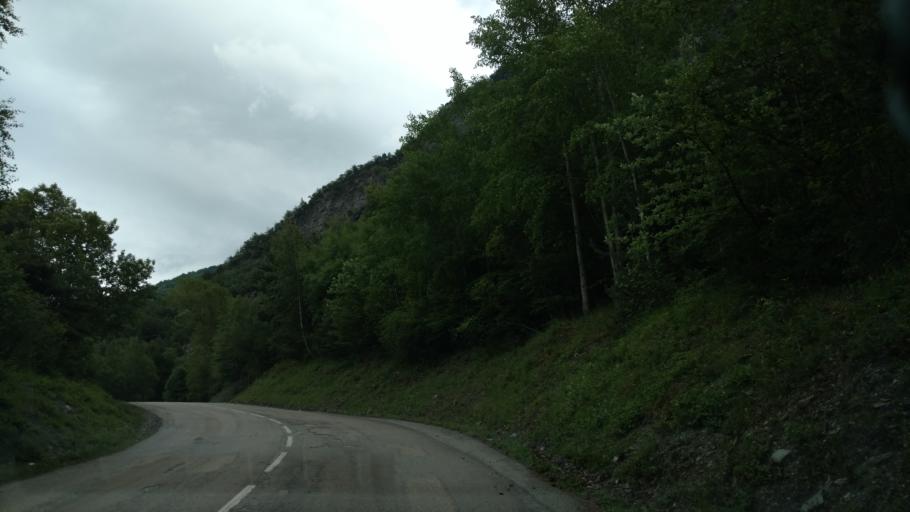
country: FR
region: Rhone-Alpes
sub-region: Departement de la Savoie
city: Villargondran
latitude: 45.2484
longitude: 6.3922
